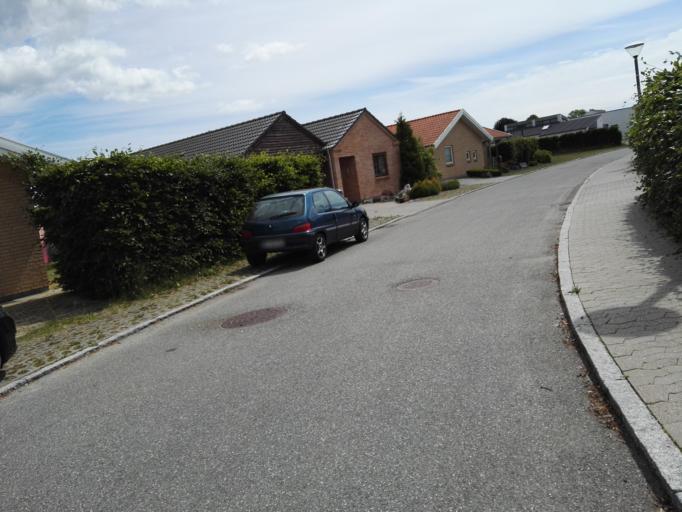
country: DK
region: Capital Region
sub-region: Egedal Kommune
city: Stenlose
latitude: 55.7637
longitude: 12.1771
